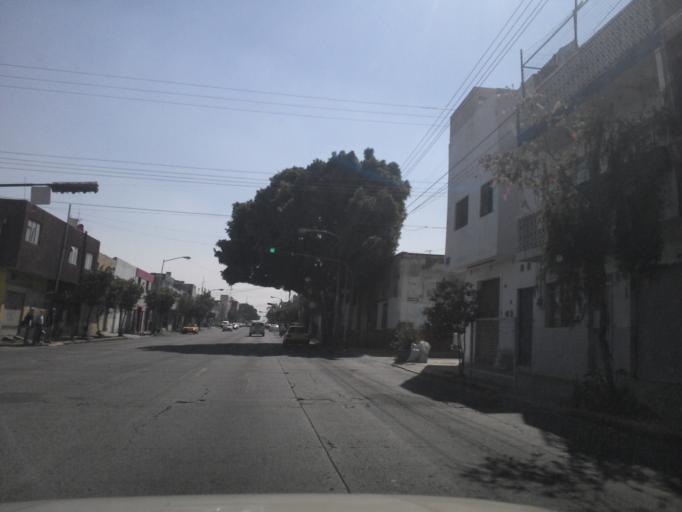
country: MX
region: Jalisco
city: Guadalajara
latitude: 20.6865
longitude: -103.3592
